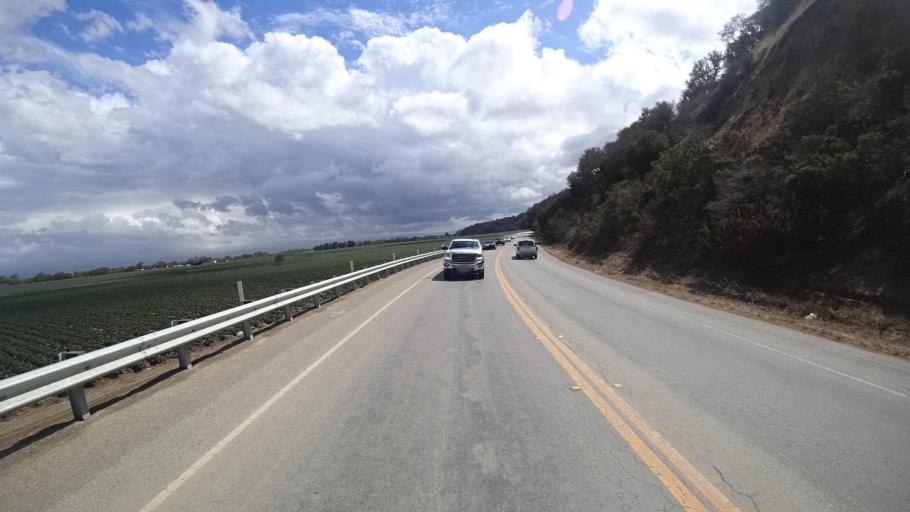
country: US
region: California
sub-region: Monterey County
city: Boronda
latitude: 36.6471
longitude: -121.7178
